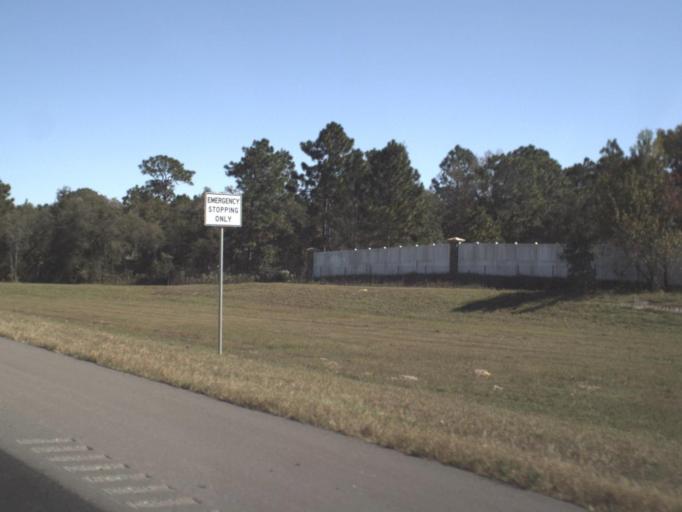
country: US
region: Florida
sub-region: Hernando County
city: Spring Hill
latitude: 28.4955
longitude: -82.4785
